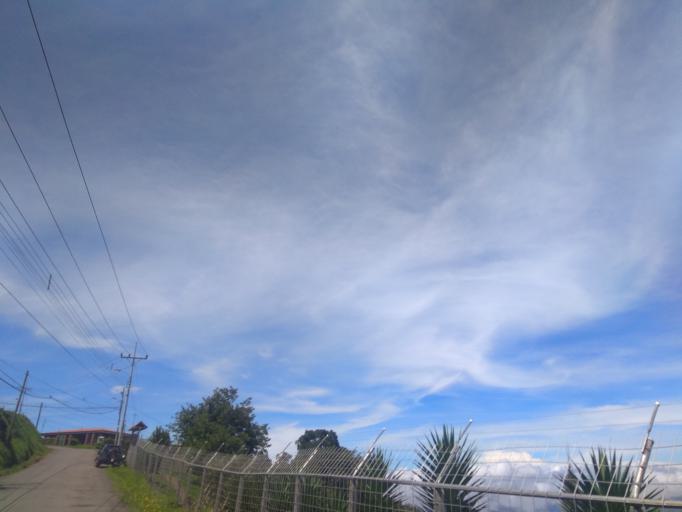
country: CR
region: Cartago
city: Cot
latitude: 9.9184
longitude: -83.8985
